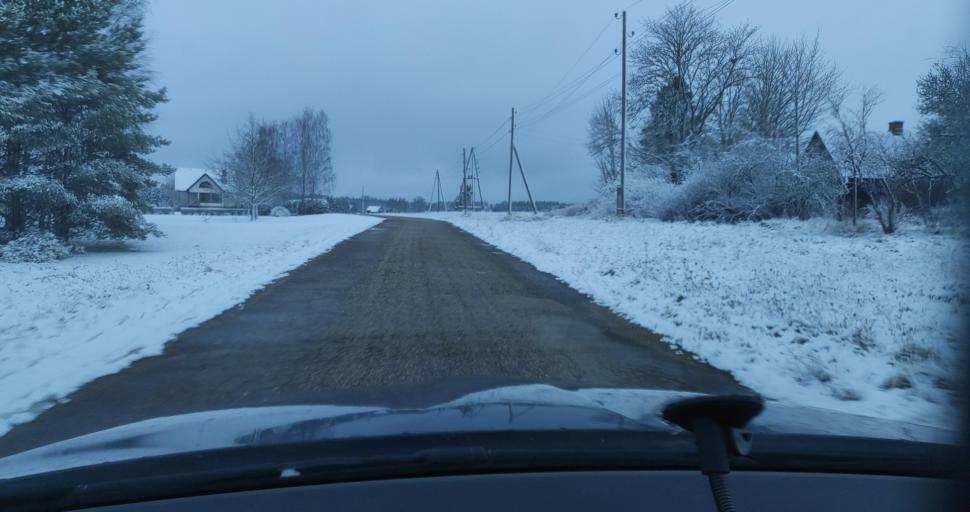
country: LV
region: Skrunda
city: Skrunda
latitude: 56.8794
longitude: 22.2403
